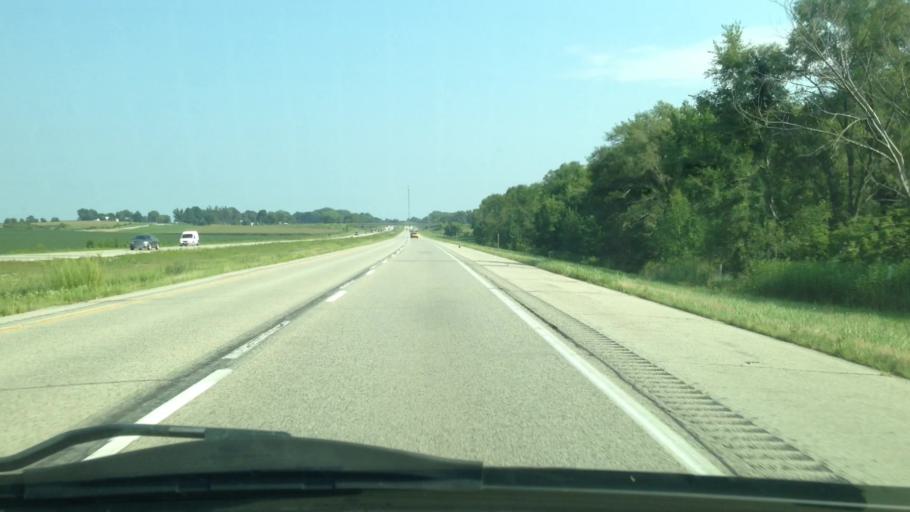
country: US
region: Iowa
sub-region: Linn County
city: Center Point
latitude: 42.1469
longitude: -91.7453
